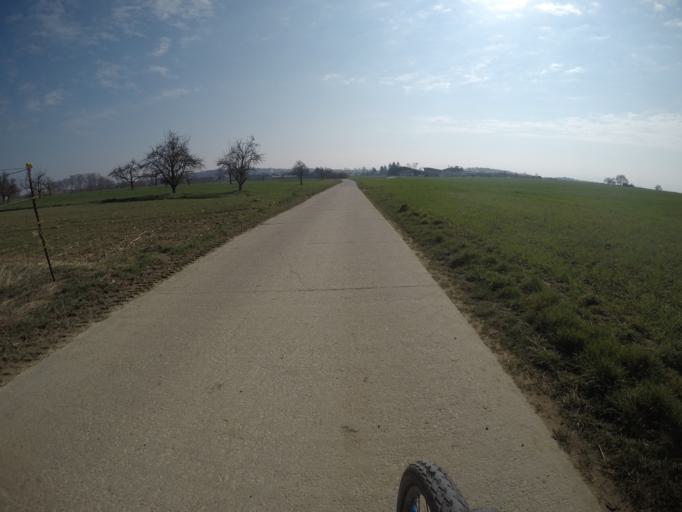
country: DE
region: Baden-Wuerttemberg
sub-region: Regierungsbezirk Stuttgart
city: Wolfschlugen
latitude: 48.6513
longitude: 9.2760
